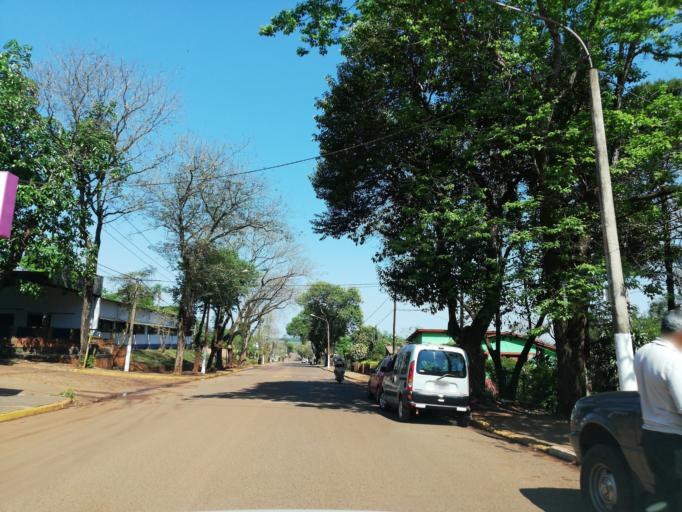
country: AR
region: Misiones
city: Puerto Eldorado
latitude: -26.4090
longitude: -54.6746
